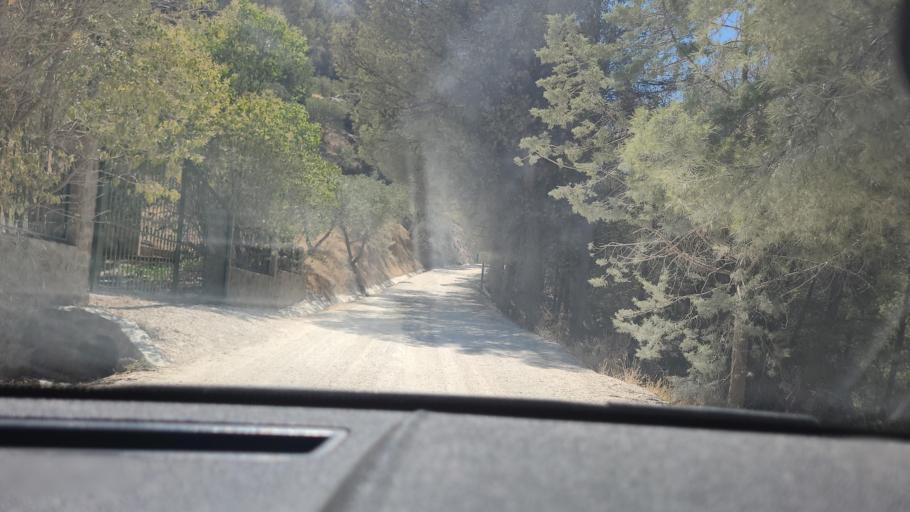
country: ES
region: Andalusia
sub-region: Provincia de Jaen
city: Belmez de la Moraleda
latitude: 37.7906
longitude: -3.4066
